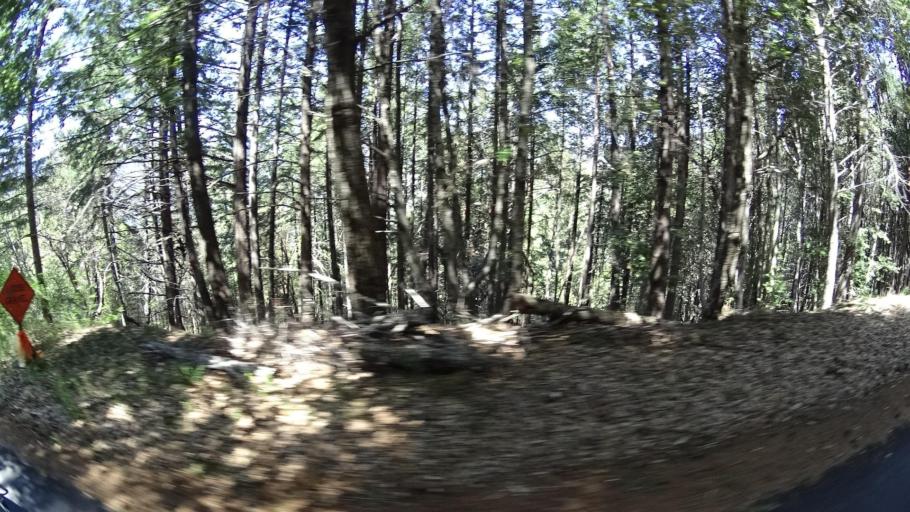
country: US
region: California
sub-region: Humboldt County
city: Rio Dell
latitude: 40.2636
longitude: -124.1095
